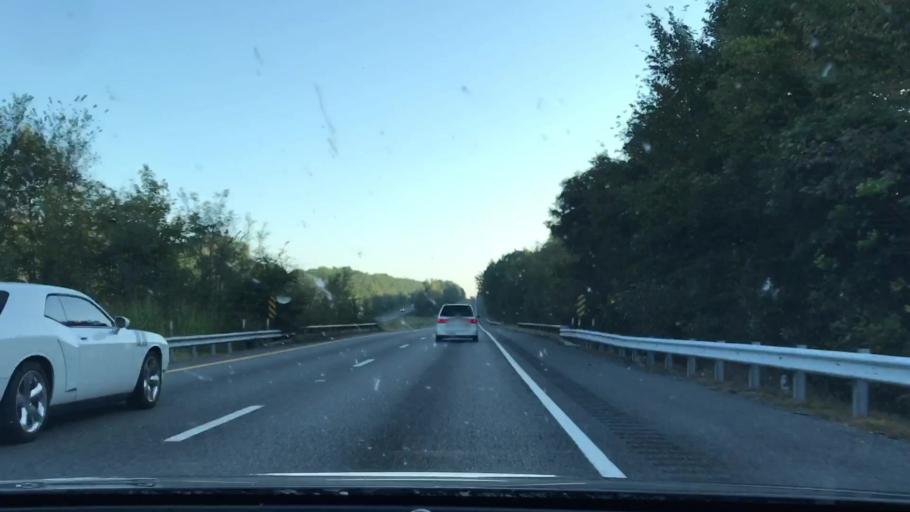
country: US
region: Tennessee
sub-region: Robertson County
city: Cross Plains
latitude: 36.5461
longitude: -86.6345
